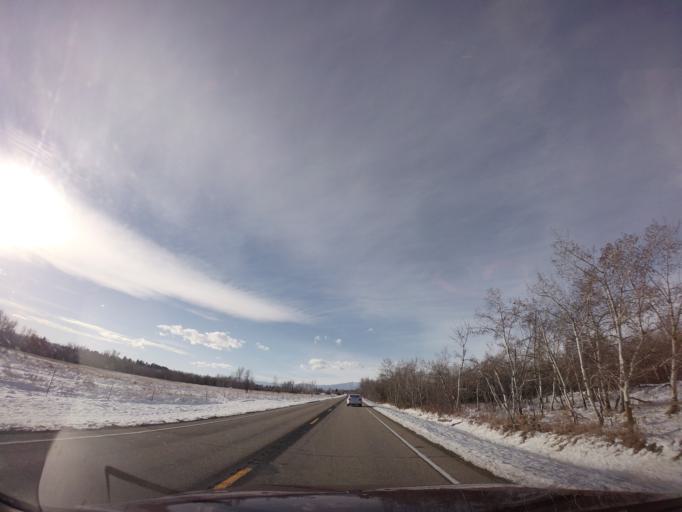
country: US
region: Montana
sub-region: Carbon County
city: Red Lodge
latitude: 45.3689
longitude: -109.1597
